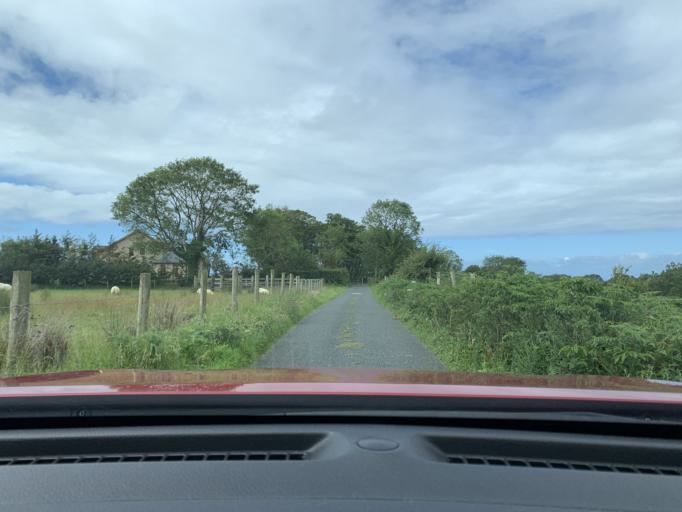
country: IE
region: Connaught
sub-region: Sligo
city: Sligo
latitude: 54.3800
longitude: -8.5042
